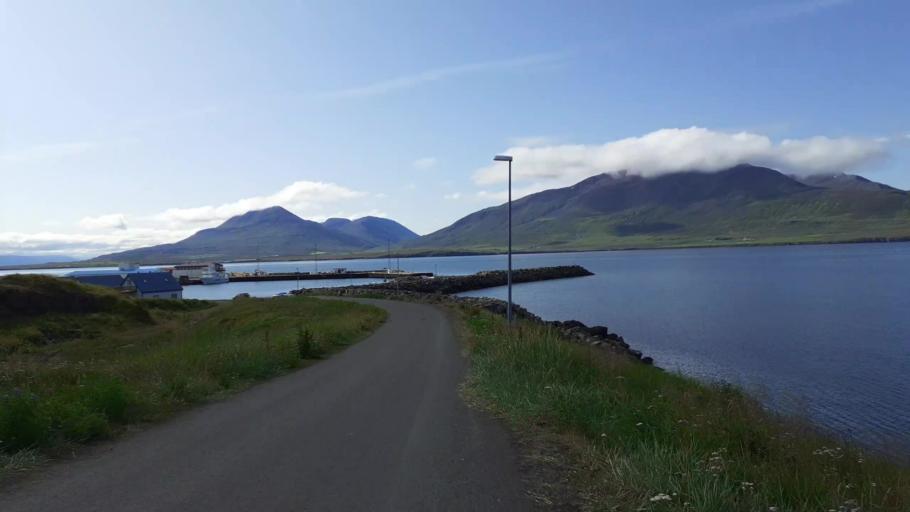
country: IS
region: Northeast
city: Dalvik
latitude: 65.9823
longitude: -18.3827
